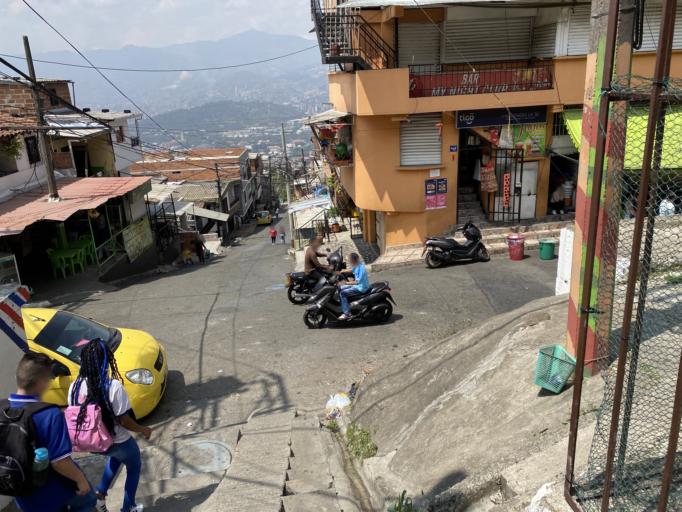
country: CO
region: Antioquia
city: Medellin
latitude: 6.2652
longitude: -75.5431
